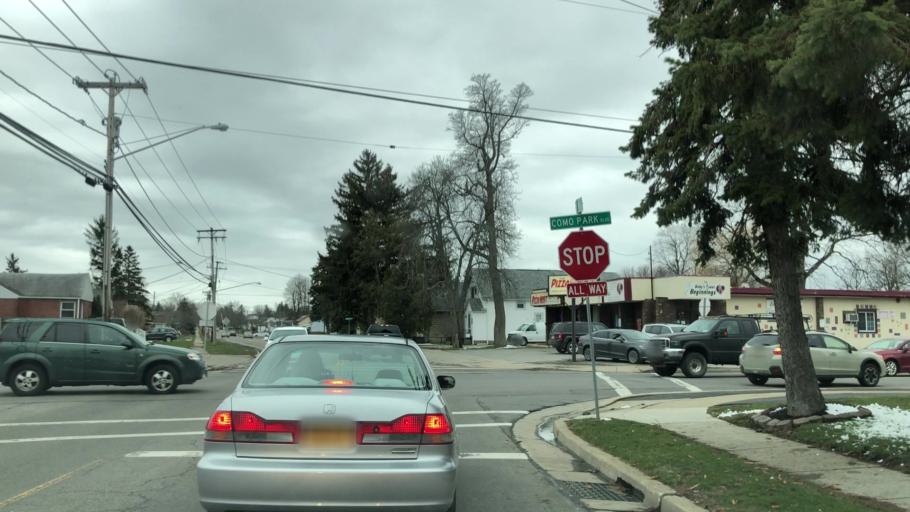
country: US
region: New York
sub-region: Erie County
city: Lancaster
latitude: 42.8930
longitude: -78.6764
